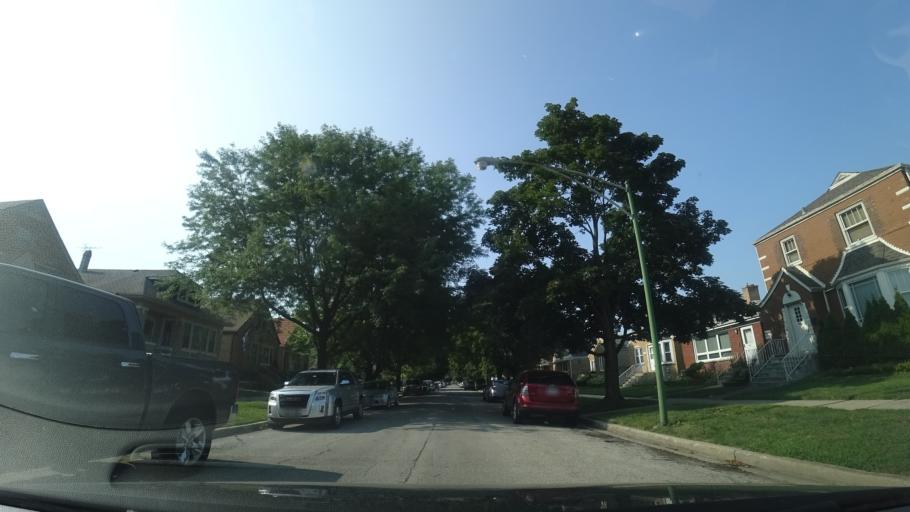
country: US
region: Illinois
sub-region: Cook County
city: Harwood Heights
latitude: 41.9719
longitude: -87.7808
